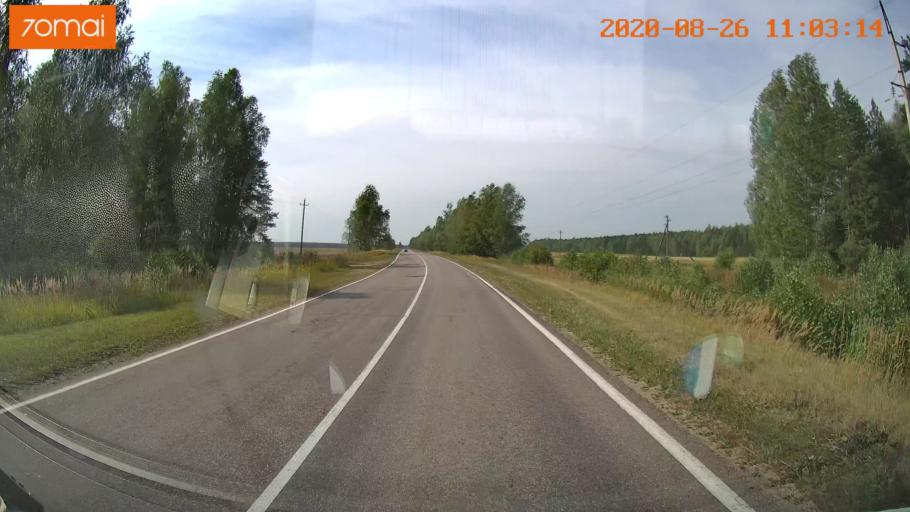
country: RU
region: Rjazan
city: Izhevskoye
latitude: 54.5427
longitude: 41.2144
